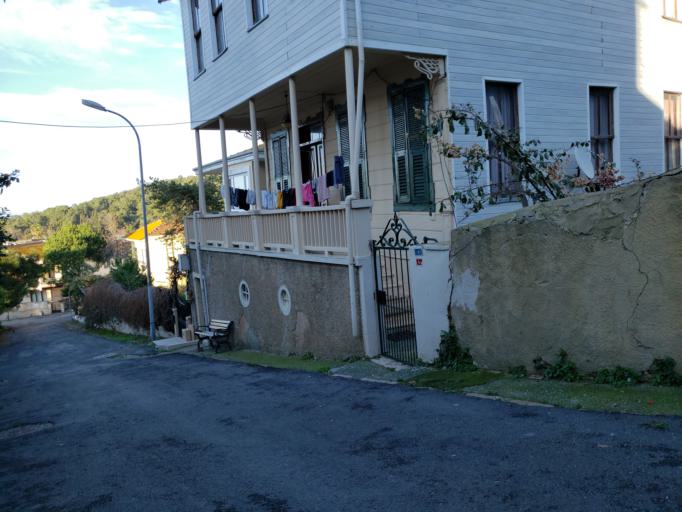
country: TR
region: Istanbul
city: Adalan
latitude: 40.8789
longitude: 29.0915
